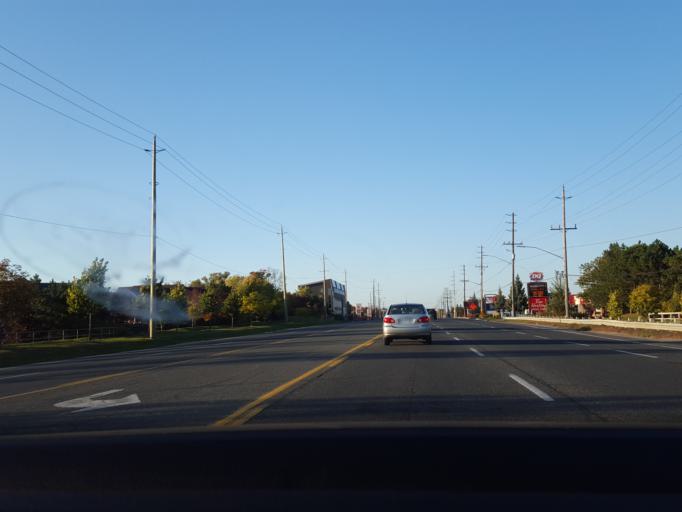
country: CA
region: Ontario
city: Newmarket
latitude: 44.0300
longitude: -79.4746
